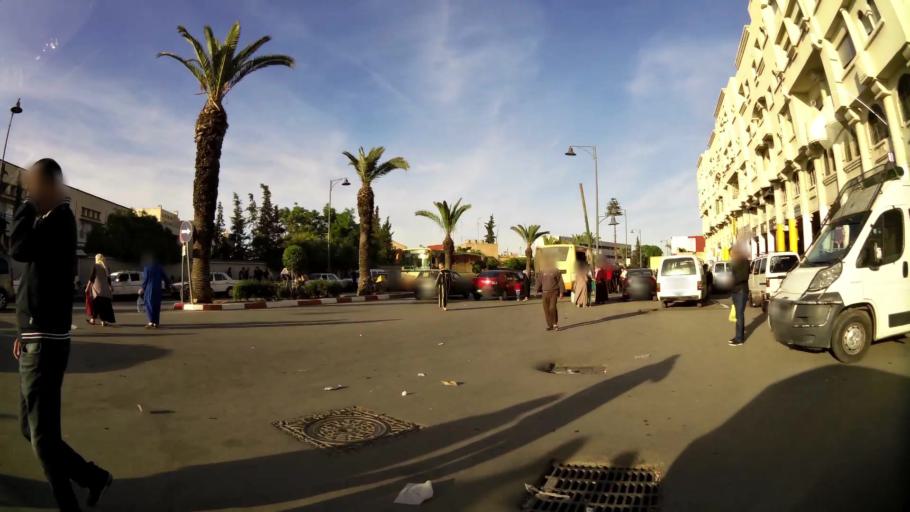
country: MA
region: Oriental
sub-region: Oujda-Angad
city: Oujda
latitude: 34.6801
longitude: -1.9073
